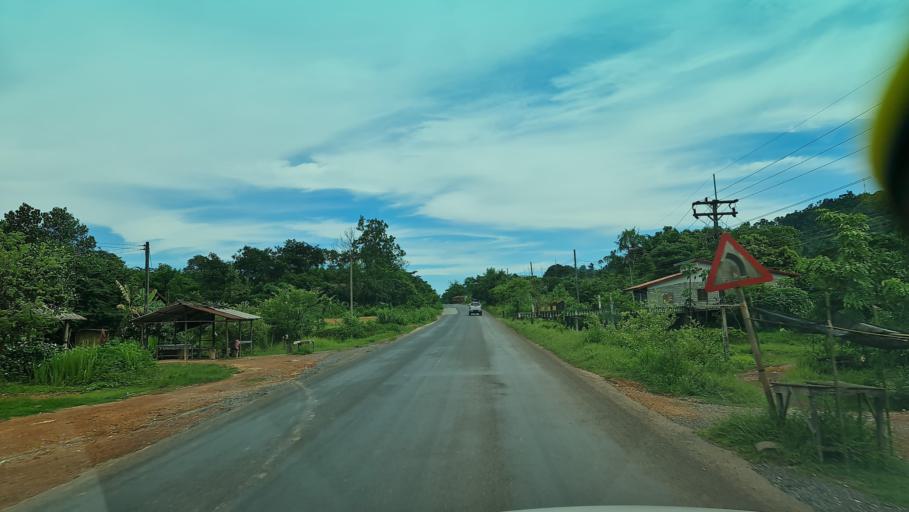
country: TH
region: Nakhon Phanom
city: Ban Phaeng
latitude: 17.9843
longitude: 104.3203
